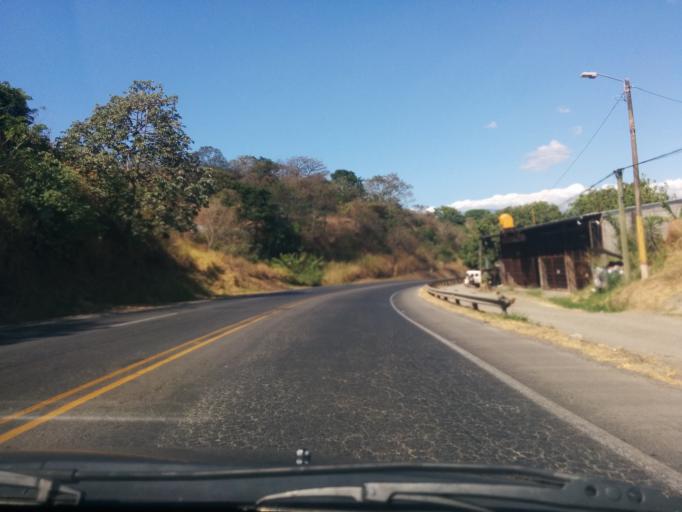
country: CR
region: Alajuela
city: Atenas
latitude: 10.0174
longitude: -84.3394
